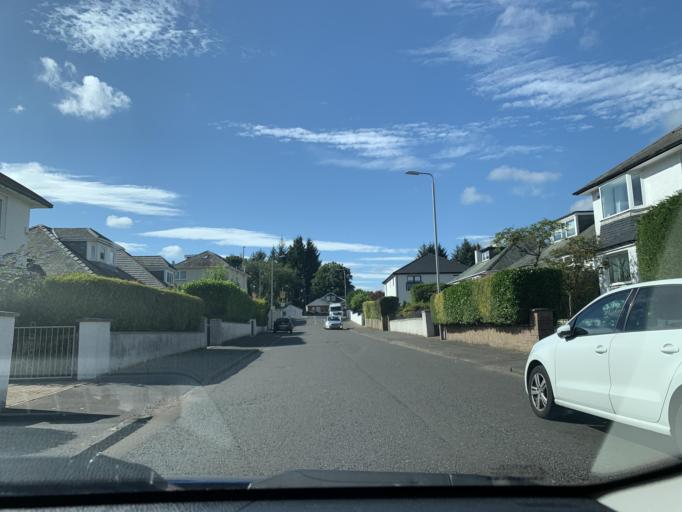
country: GB
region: Scotland
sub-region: East Renfrewshire
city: Newton Mearns
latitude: 55.7784
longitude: -4.3195
